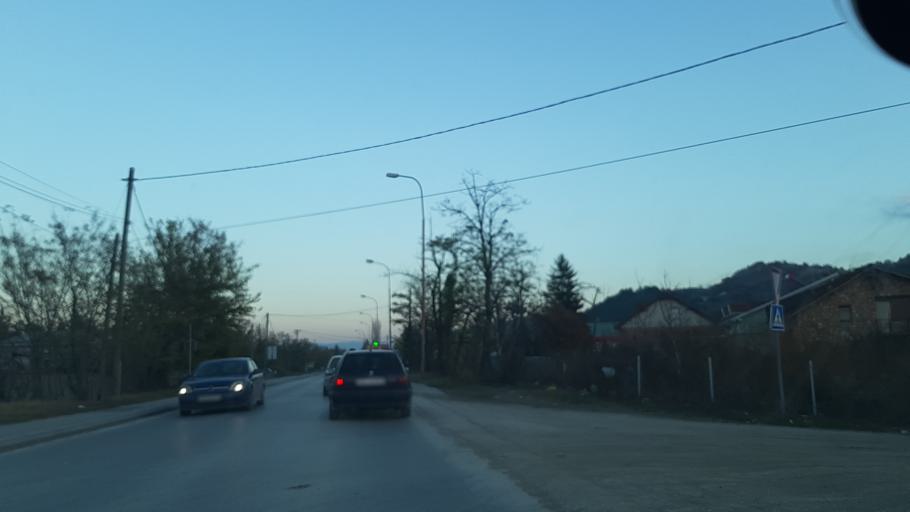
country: MK
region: Kisela Voda
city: Kisela Voda
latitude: 41.9393
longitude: 21.5056
